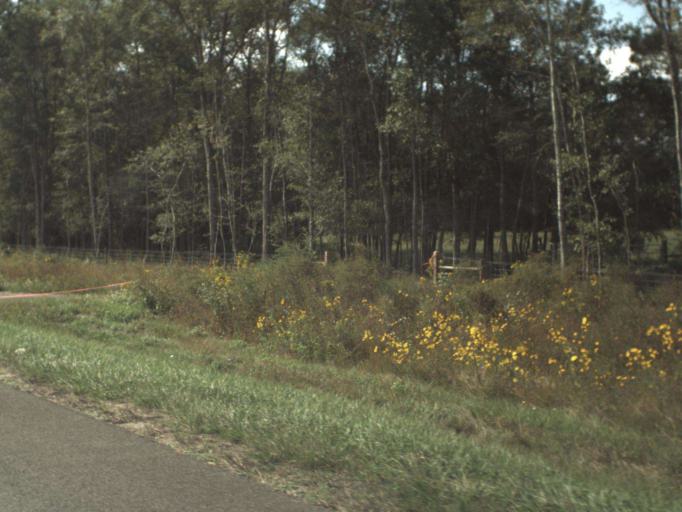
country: US
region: Florida
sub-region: Holmes County
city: Bonifay
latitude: 30.5914
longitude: -85.7876
